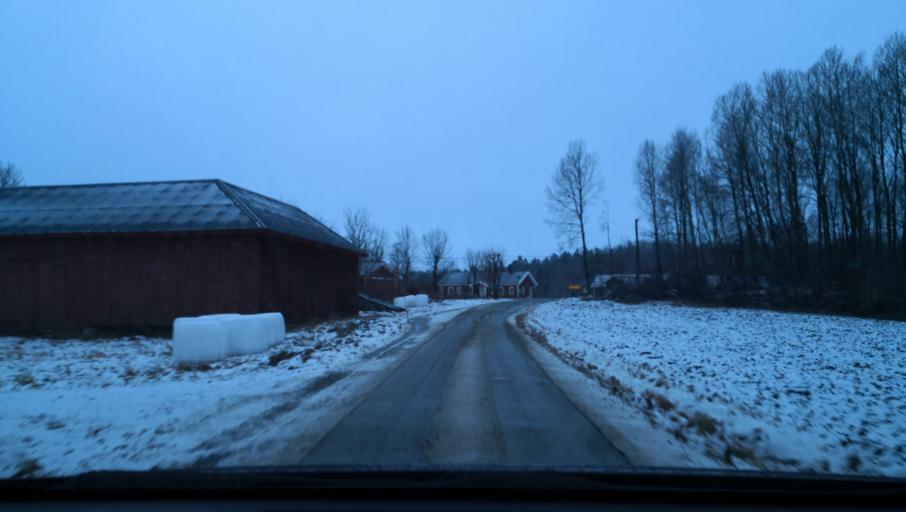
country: SE
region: Vaestmanland
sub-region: Kungsors Kommun
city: Kungsoer
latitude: 59.4026
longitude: 16.2038
